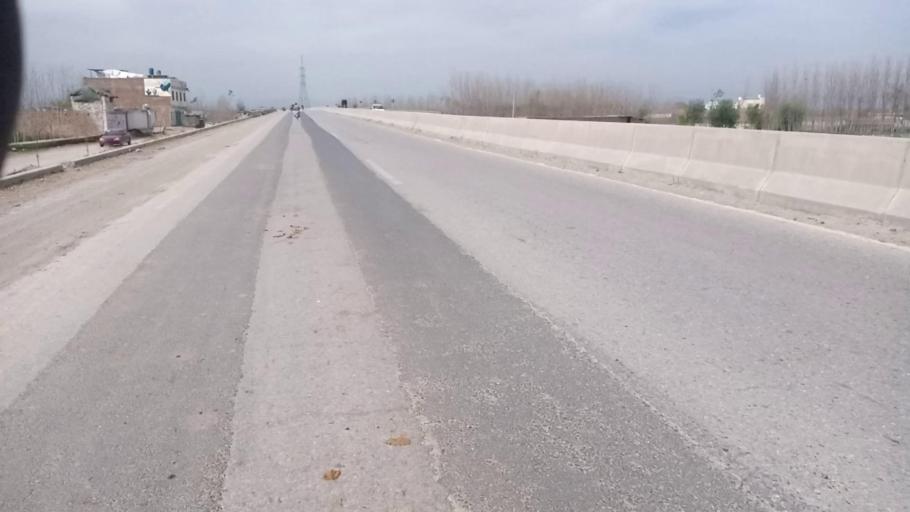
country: PK
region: Khyber Pakhtunkhwa
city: Peshawar
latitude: 34.0526
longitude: 71.6127
